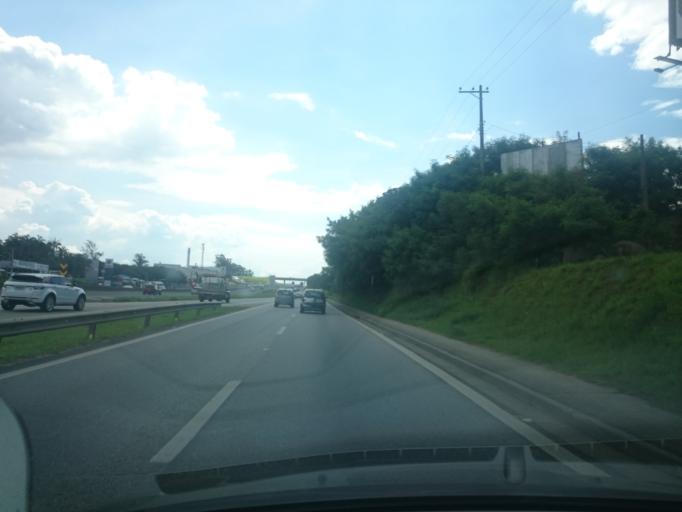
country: BR
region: Sao Paulo
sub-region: Sorocaba
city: Sorocaba
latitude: -23.5324
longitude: -47.4810
